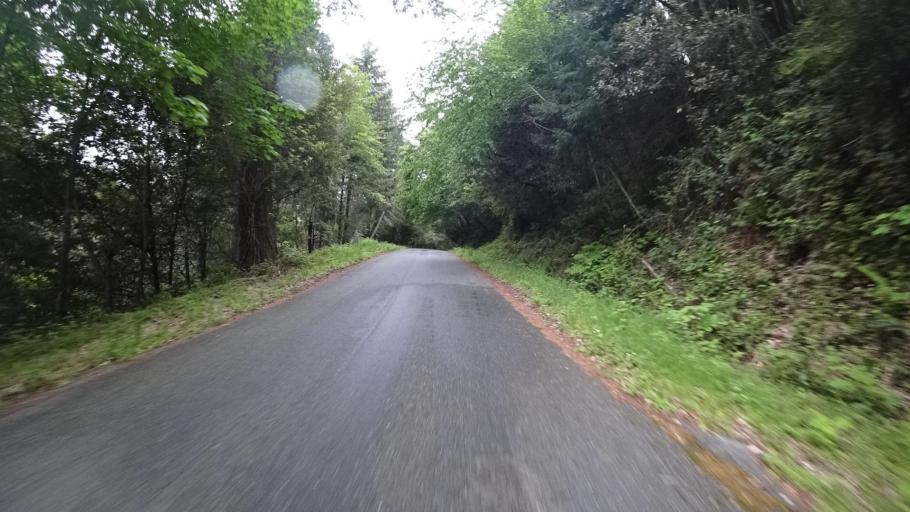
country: US
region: California
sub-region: Humboldt County
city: Willow Creek
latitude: 41.2049
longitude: -123.7565
